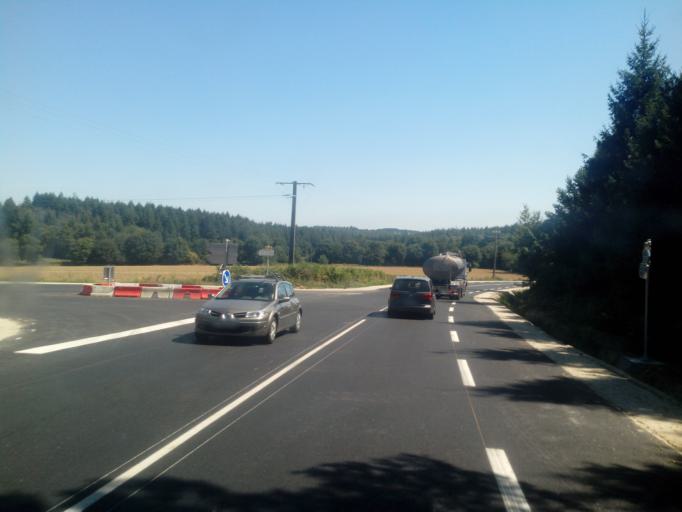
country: FR
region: Brittany
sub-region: Departement du Morbihan
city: Guillac
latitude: 47.8725
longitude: -2.4687
